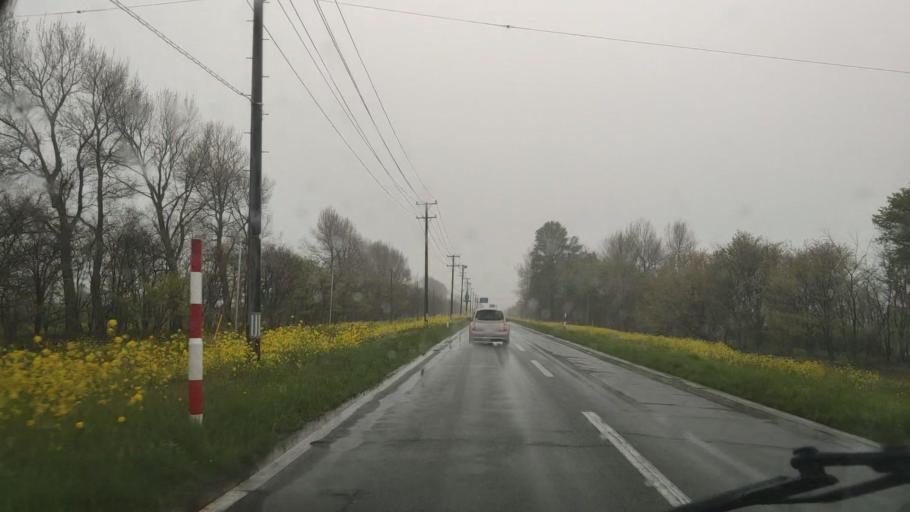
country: JP
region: Akita
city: Tenno
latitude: 39.9761
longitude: 139.9462
